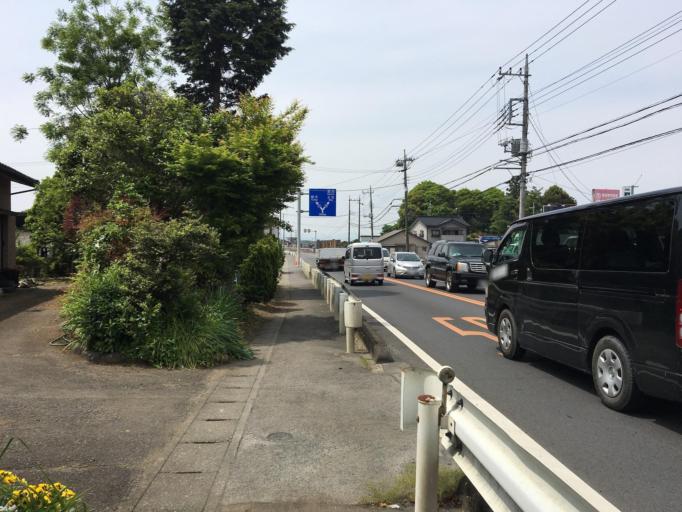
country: JP
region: Tochigi
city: Oyama
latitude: 36.3580
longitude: 139.8129
